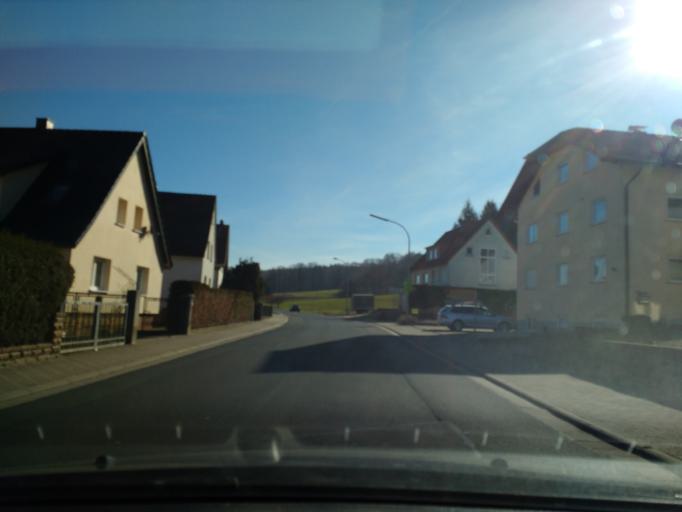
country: DE
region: Bavaria
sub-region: Regierungsbezirk Unterfranken
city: Geiselbach
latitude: 50.1384
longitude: 9.1465
